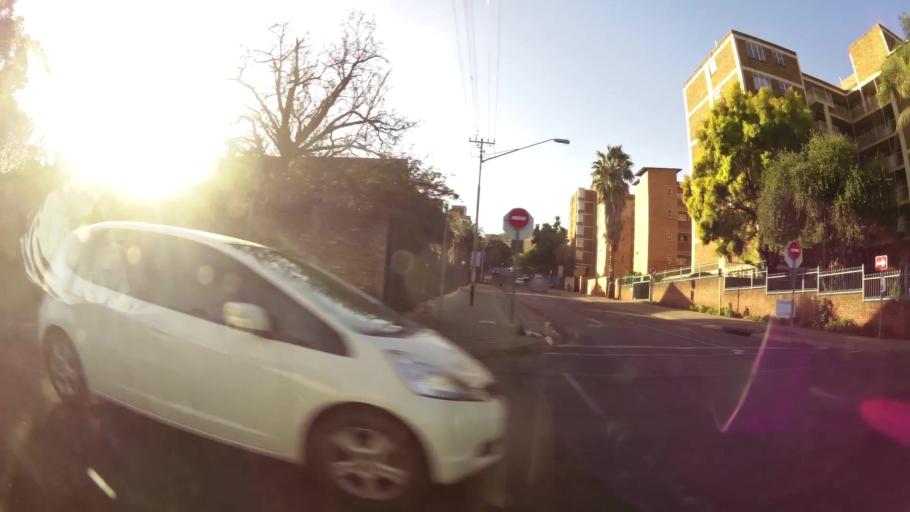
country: ZA
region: Gauteng
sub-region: City of Tshwane Metropolitan Municipality
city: Pretoria
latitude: -25.6985
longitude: 28.2023
